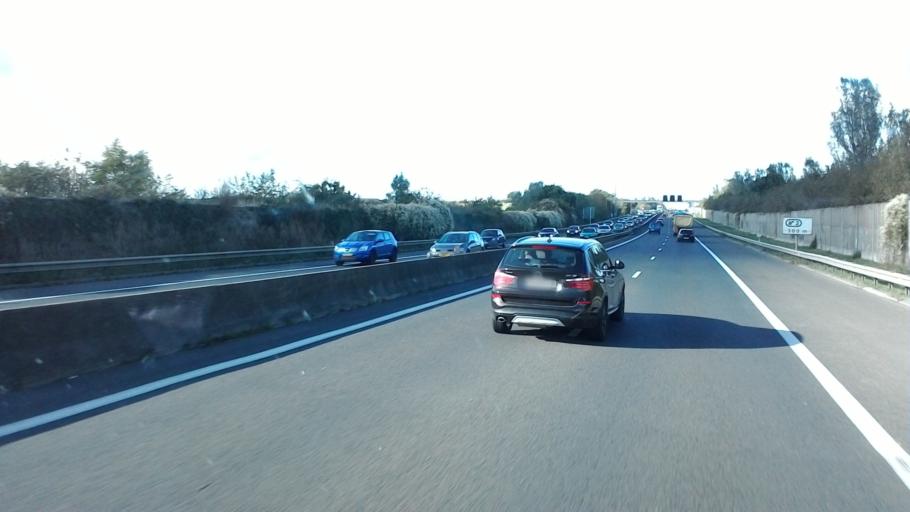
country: LU
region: Luxembourg
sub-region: Canton d'Esch-sur-Alzette
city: Bettembourg
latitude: 49.5233
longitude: 6.1158
